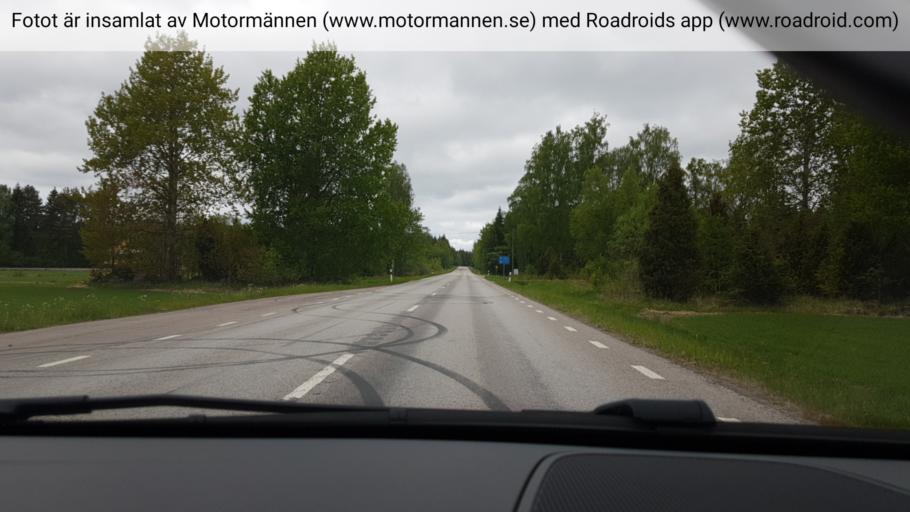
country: SE
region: Uppsala
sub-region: Tierps Kommun
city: Tierp
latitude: 60.3617
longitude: 17.3161
